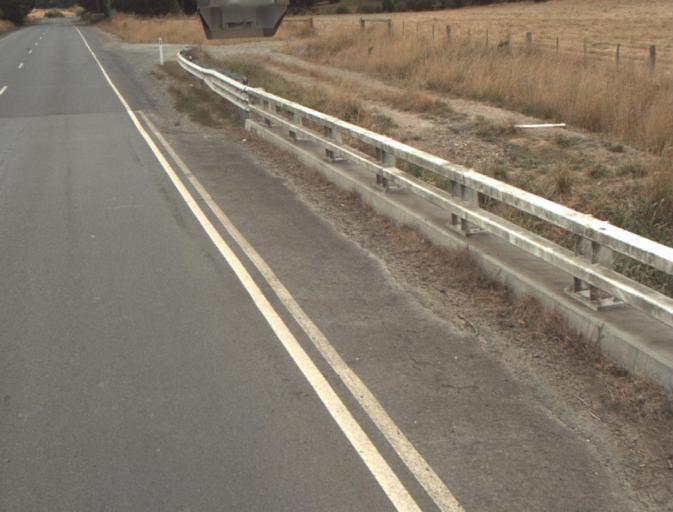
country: AU
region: Tasmania
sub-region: Launceston
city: Mayfield
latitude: -41.2320
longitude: 147.2102
